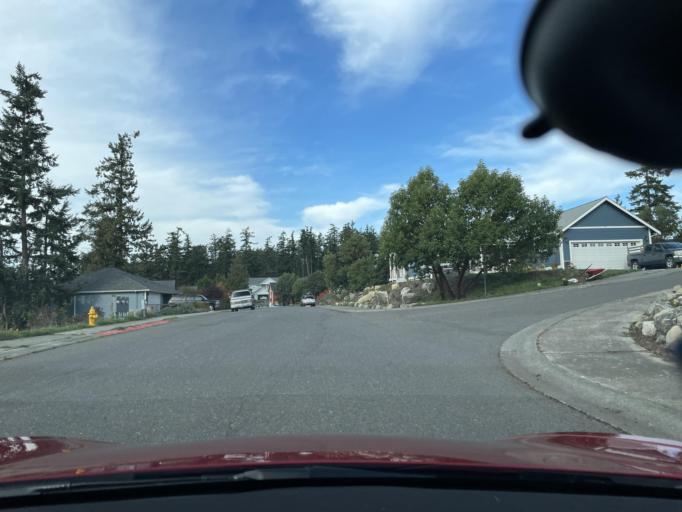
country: US
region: Washington
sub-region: San Juan County
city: Friday Harbor
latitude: 48.5414
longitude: -123.0317
